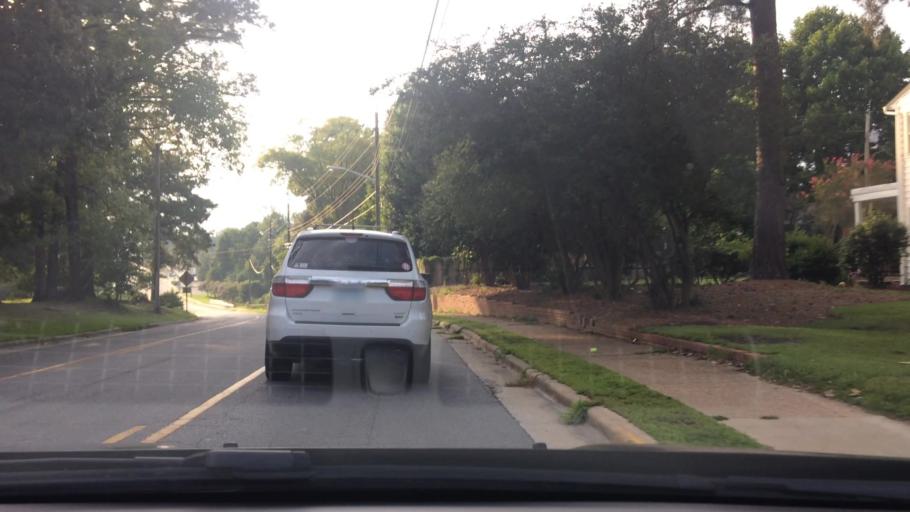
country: US
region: North Carolina
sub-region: Pitt County
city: Greenville
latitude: 35.6000
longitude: -77.3661
